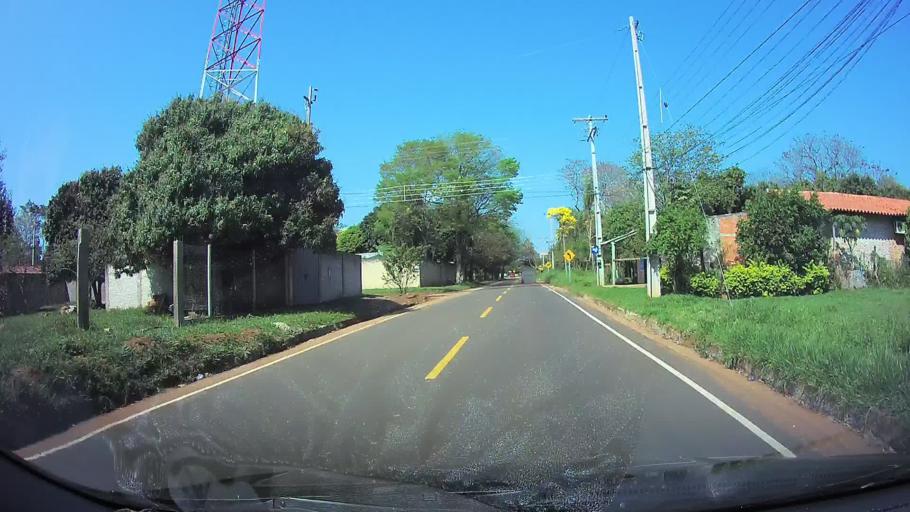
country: PY
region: Central
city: Limpio
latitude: -25.2364
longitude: -57.4837
